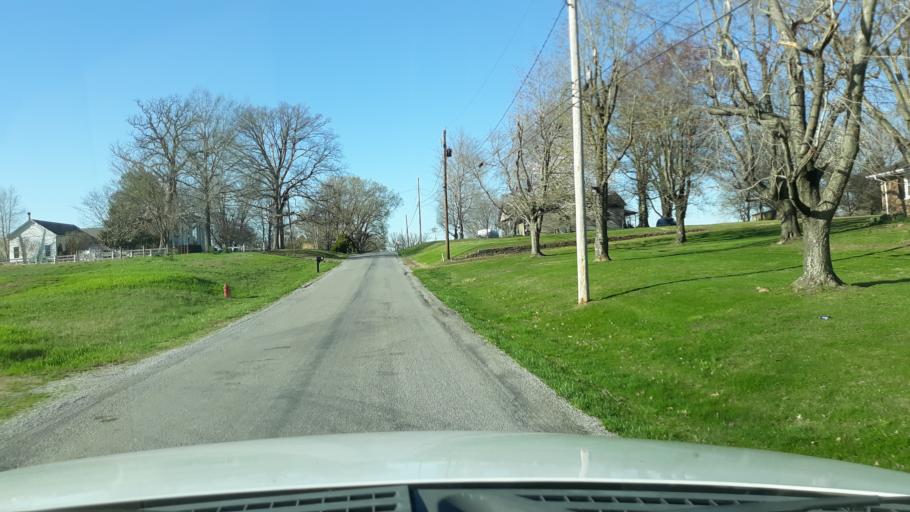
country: US
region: Illinois
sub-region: Saline County
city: Harrisburg
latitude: 37.7510
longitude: -88.5680
